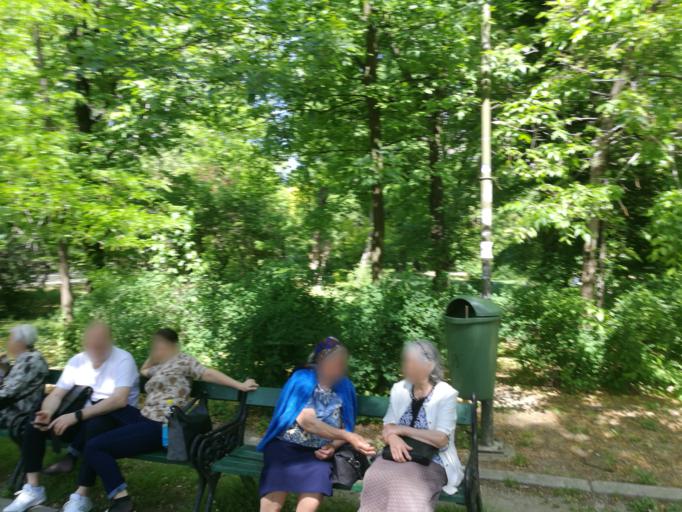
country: RO
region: Bucuresti
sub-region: Municipiul Bucuresti
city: Bucuresti
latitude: 44.4363
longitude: 26.0920
